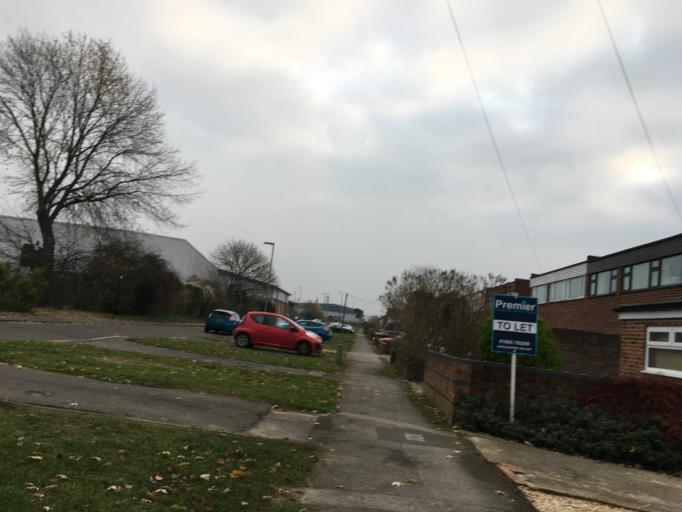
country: GB
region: England
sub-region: Oxfordshire
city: Cowley
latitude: 51.7257
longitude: -1.1978
